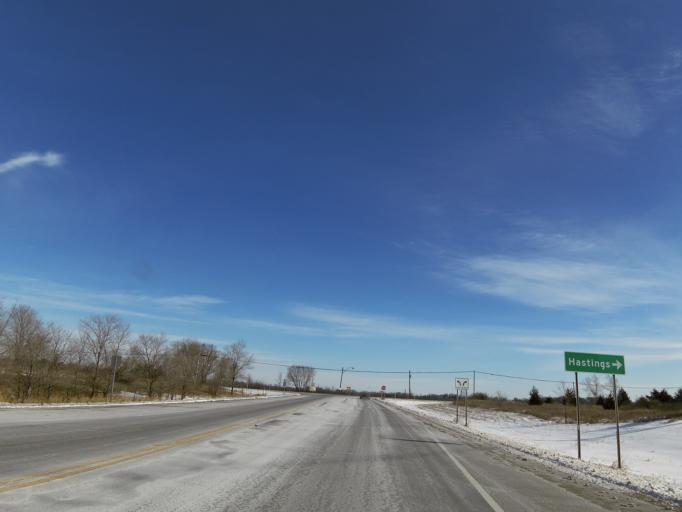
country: US
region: Minnesota
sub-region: Washington County
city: Cottage Grove
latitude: 44.7424
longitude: -92.9887
